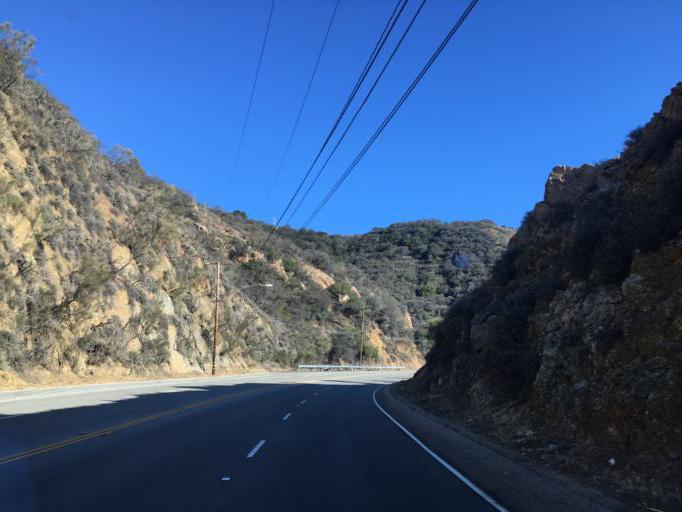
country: US
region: California
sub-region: Los Angeles County
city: Malibu
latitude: 34.0494
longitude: -118.7981
